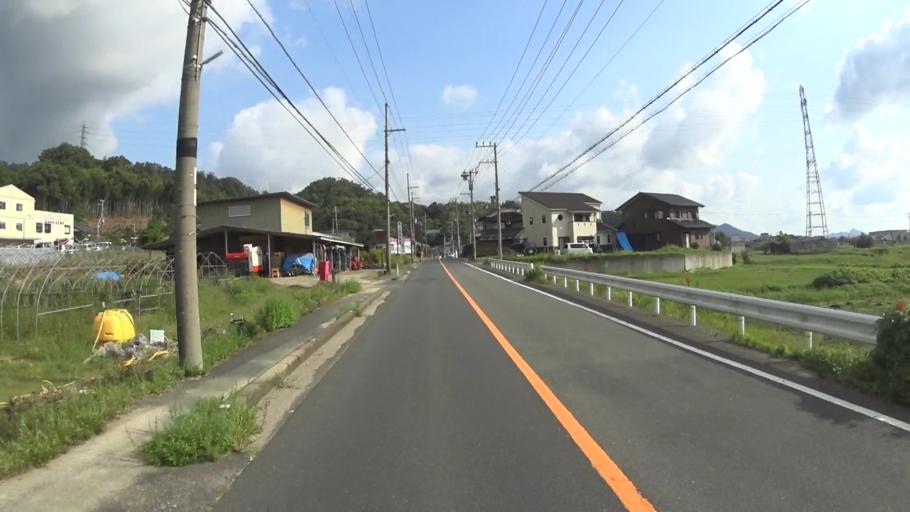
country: JP
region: Kyoto
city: Miyazu
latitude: 35.5585
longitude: 135.1406
